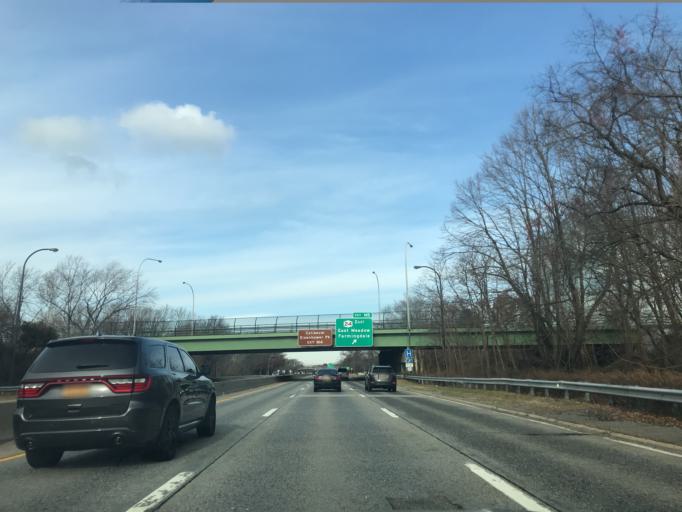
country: US
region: New York
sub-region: Nassau County
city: Uniondale
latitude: 40.7173
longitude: -73.5805
